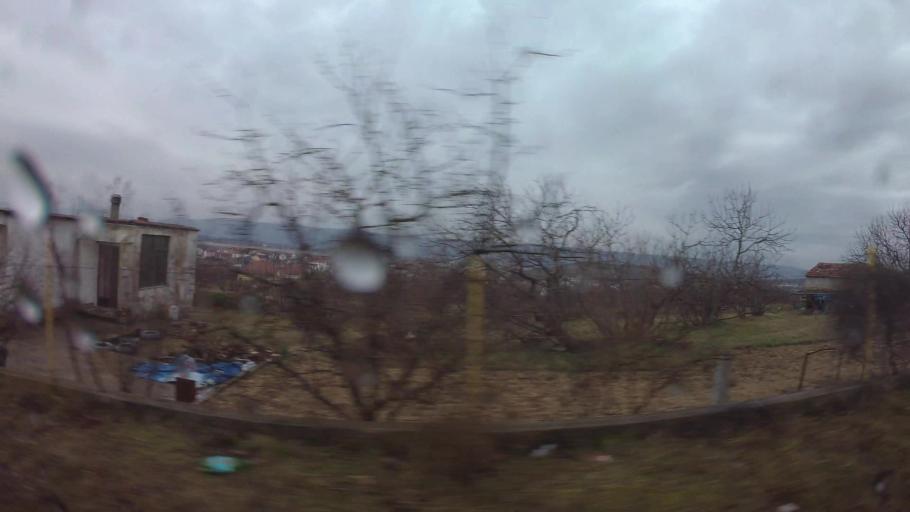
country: BA
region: Federation of Bosnia and Herzegovina
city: Blagaj
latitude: 43.2917
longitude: 17.8587
